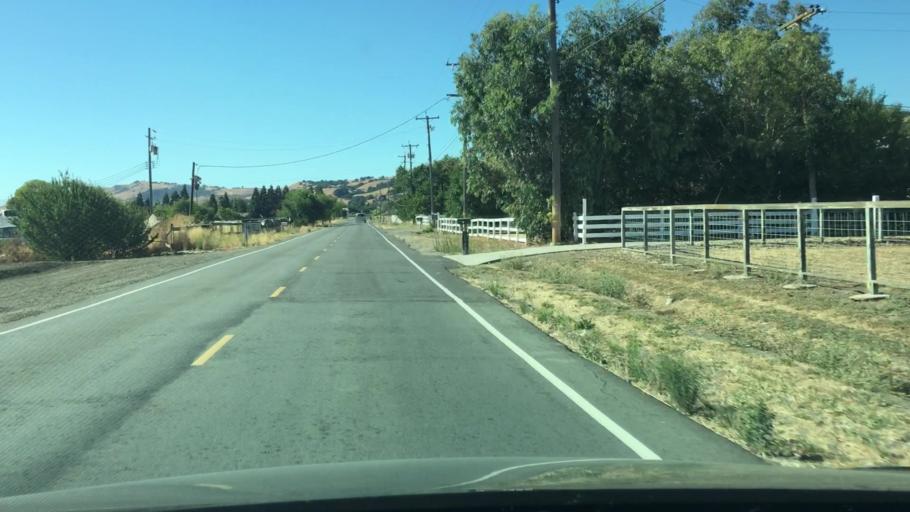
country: US
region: California
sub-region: Santa Clara County
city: San Martin
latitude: 37.1248
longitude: -121.5982
